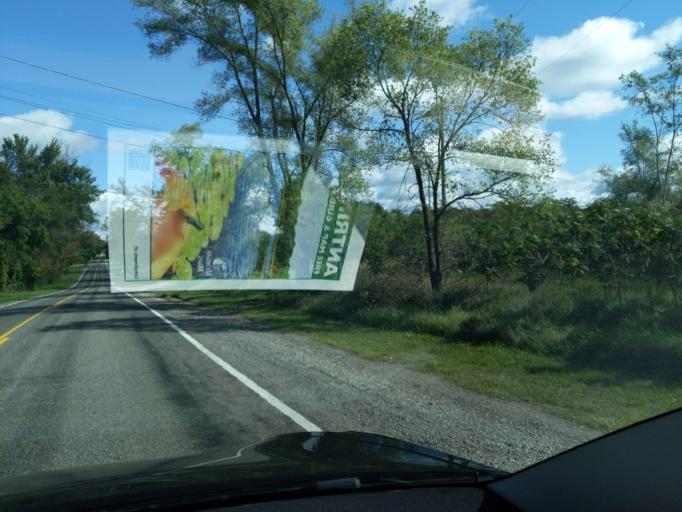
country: US
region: Michigan
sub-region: Antrim County
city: Elk Rapids
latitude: 44.9341
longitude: -85.3625
